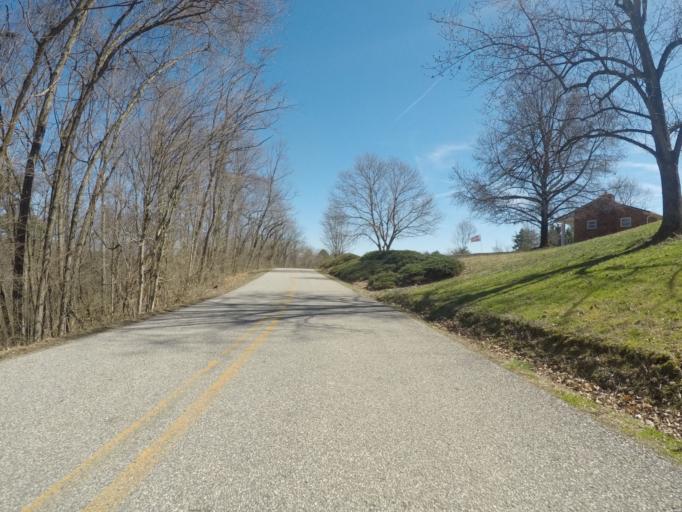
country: US
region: West Virginia
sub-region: Cabell County
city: Huntington
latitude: 38.4435
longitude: -82.4871
